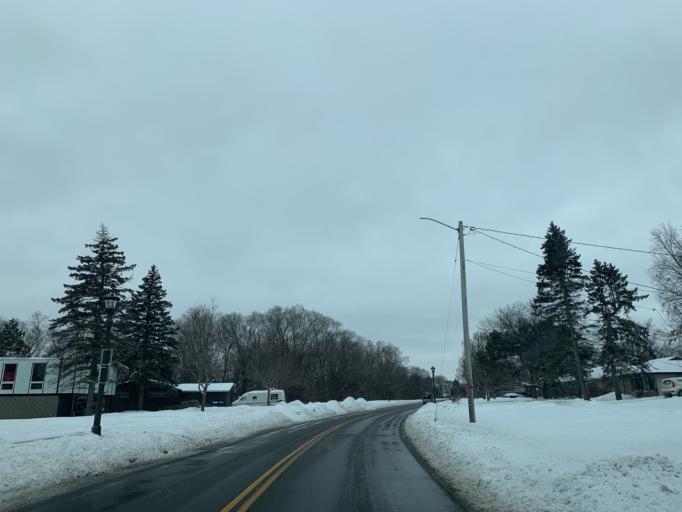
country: US
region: Minnesota
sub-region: Ramsey County
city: Roseville
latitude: 44.9885
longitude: -93.1139
